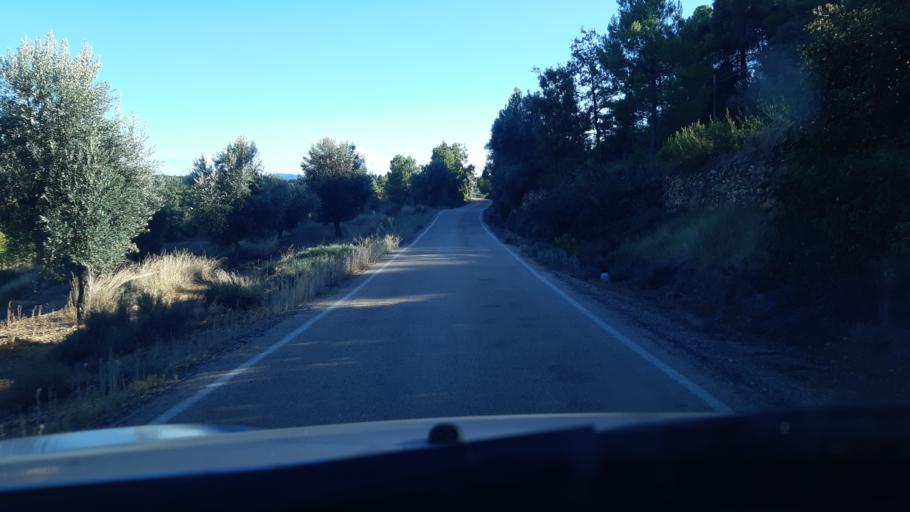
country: ES
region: Aragon
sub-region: Provincia de Teruel
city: Fornoles
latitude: 40.9062
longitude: -0.0123
